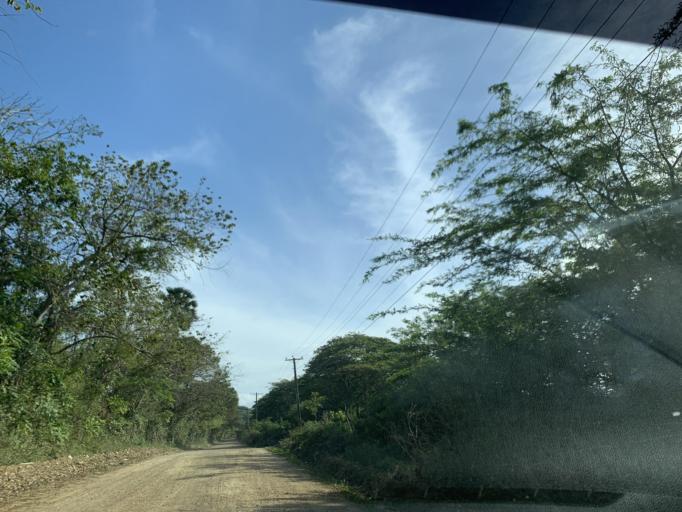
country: DO
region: Puerto Plata
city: Luperon
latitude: 19.8810
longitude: -70.9257
